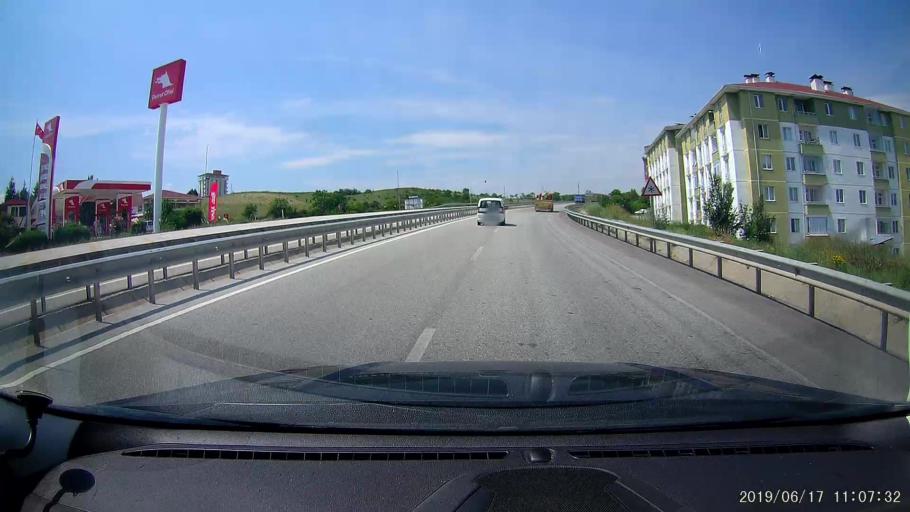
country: TR
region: Kastamonu
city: Tosya
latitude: 41.0013
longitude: 34.0536
